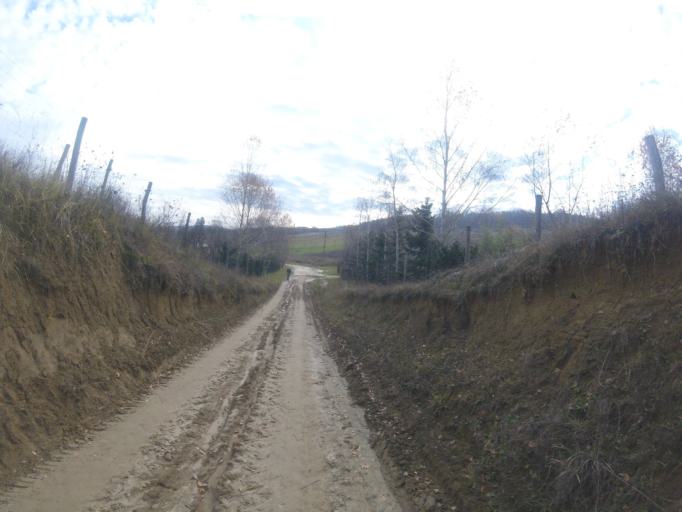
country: HU
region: Tolna
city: Bonyhad
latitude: 46.2468
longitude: 18.6080
